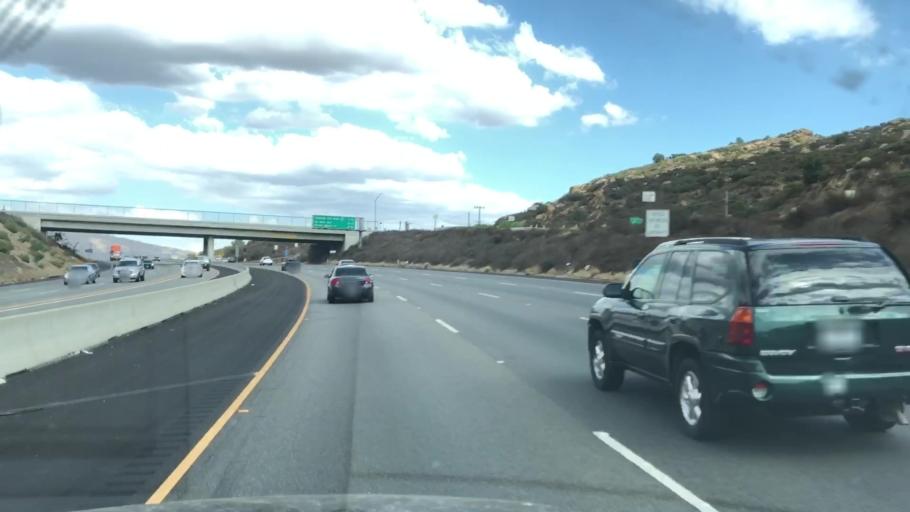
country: US
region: California
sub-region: Los Angeles County
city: Chatsworth
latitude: 34.2664
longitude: -118.6361
